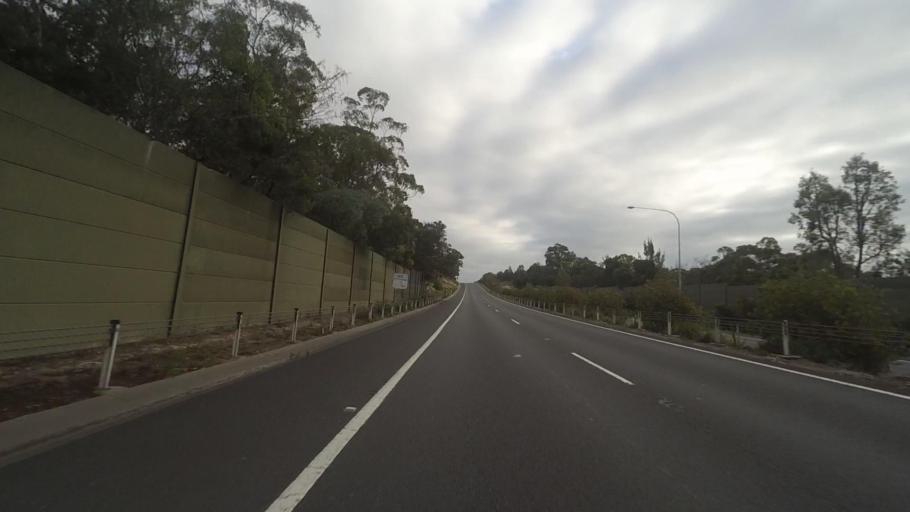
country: AU
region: New South Wales
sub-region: Sutherland Shire
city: Menai
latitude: -34.0184
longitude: 151.0091
